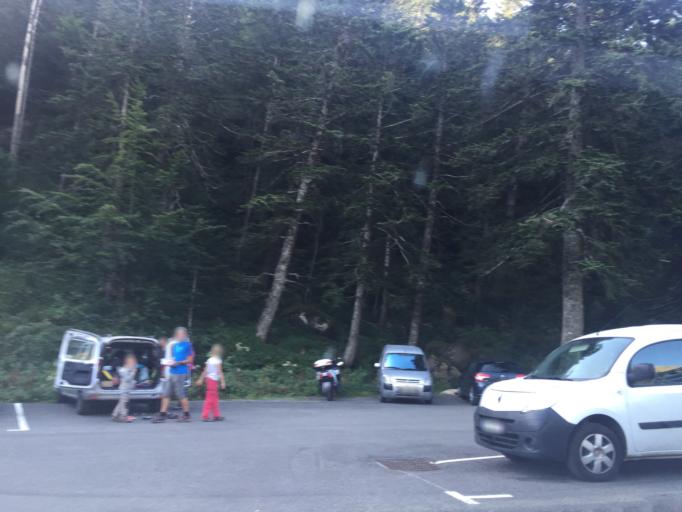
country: FR
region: Midi-Pyrenees
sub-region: Departement des Hautes-Pyrenees
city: Cauterets
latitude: 42.8516
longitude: -0.1362
